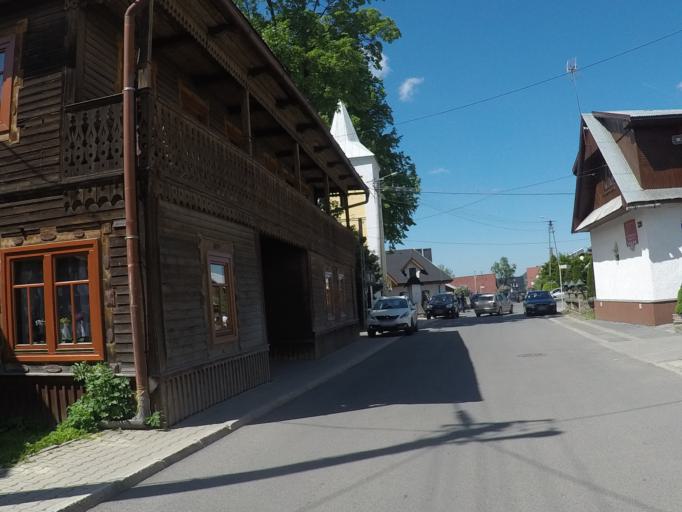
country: PL
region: Lesser Poland Voivodeship
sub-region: Powiat tatrzanski
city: Bukowina Tatrzanska
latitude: 49.3421
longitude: 20.1361
